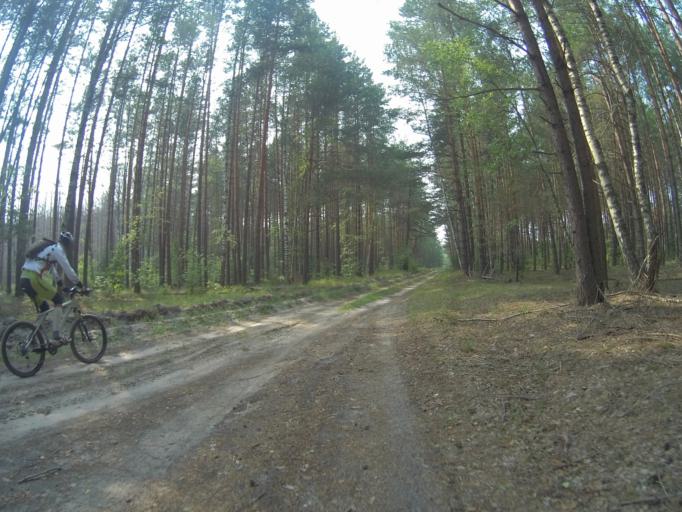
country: RU
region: Vladimir
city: Vorsha
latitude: 55.9679
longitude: 40.1684
